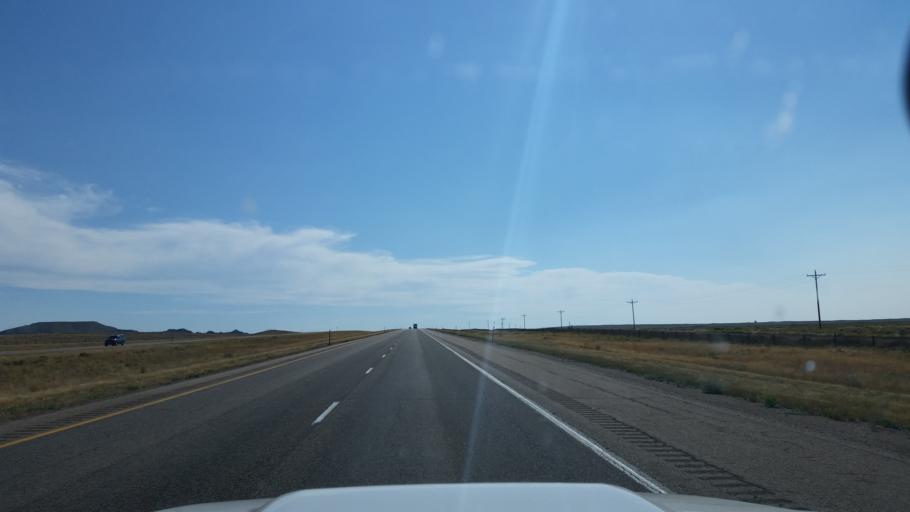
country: US
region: Wyoming
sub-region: Uinta County
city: Lyman
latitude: 41.4418
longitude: -110.0901
